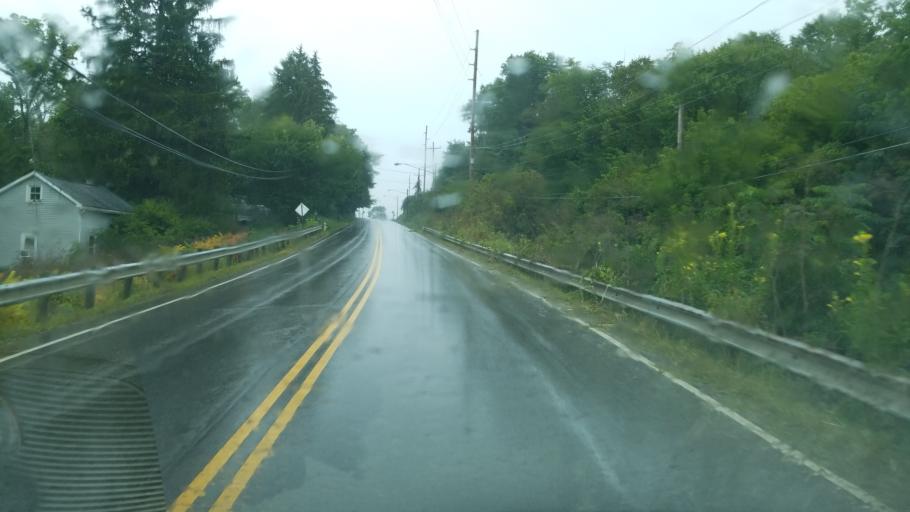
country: US
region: Ohio
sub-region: Richland County
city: Mansfield
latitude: 40.7258
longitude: -82.5123
